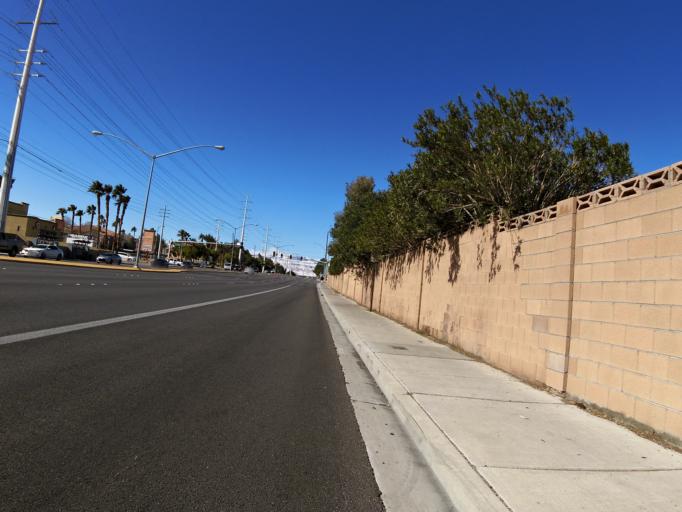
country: US
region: Nevada
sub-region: Clark County
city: Spring Valley
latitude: 36.1152
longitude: -115.2150
